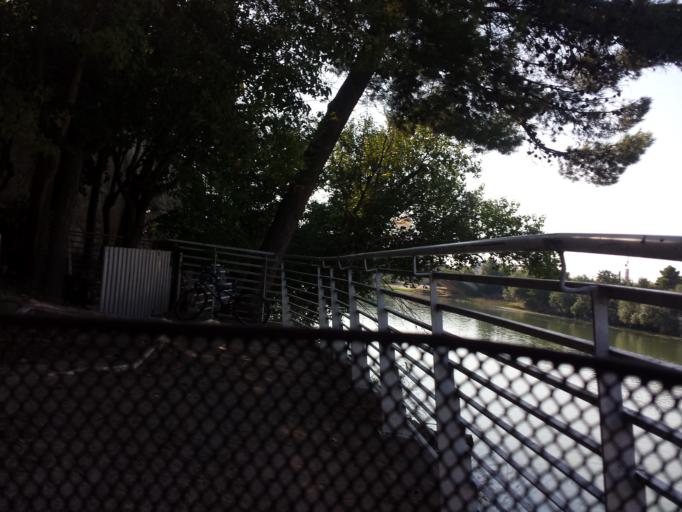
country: ES
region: Aragon
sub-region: Provincia de Zaragoza
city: Zaragoza
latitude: 41.6574
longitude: -0.8785
